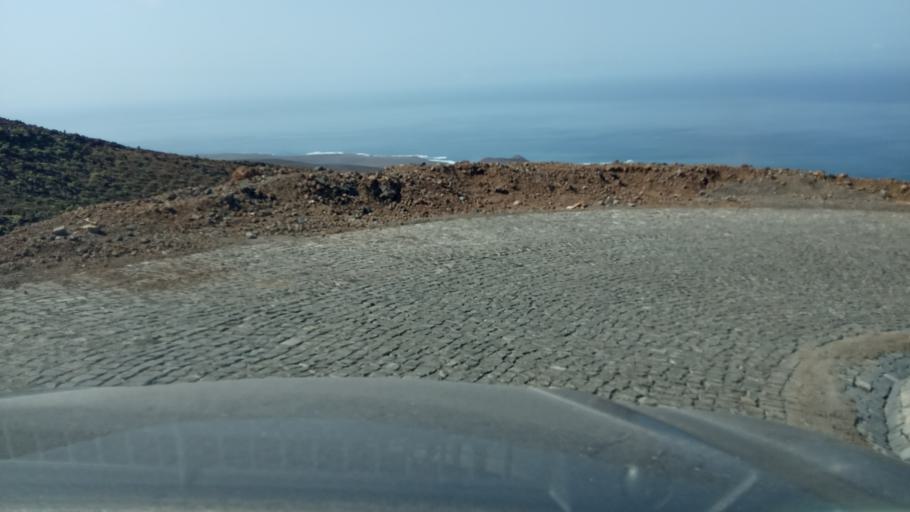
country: CV
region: Porto Novo
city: Porto Novo
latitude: 16.9520
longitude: -25.3020
